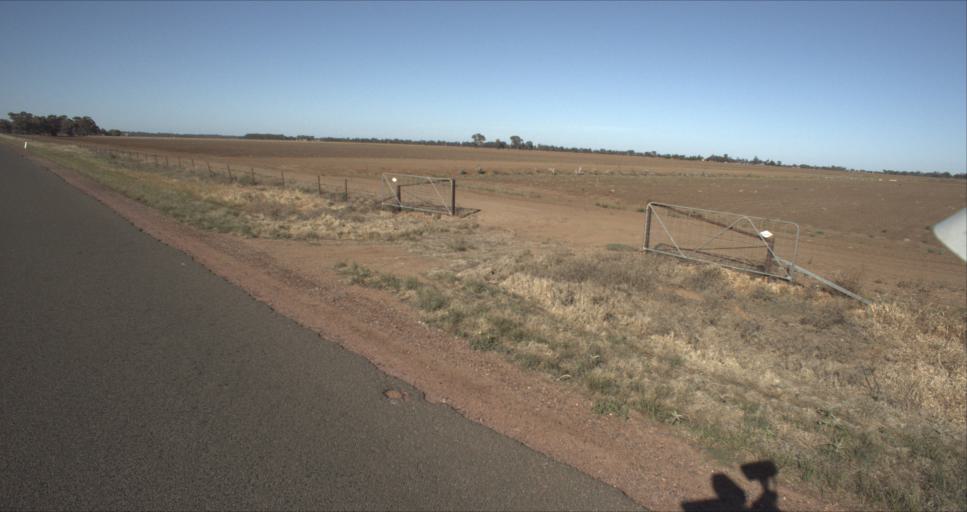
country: AU
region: New South Wales
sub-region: Leeton
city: Leeton
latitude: -34.5715
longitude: 146.2634
